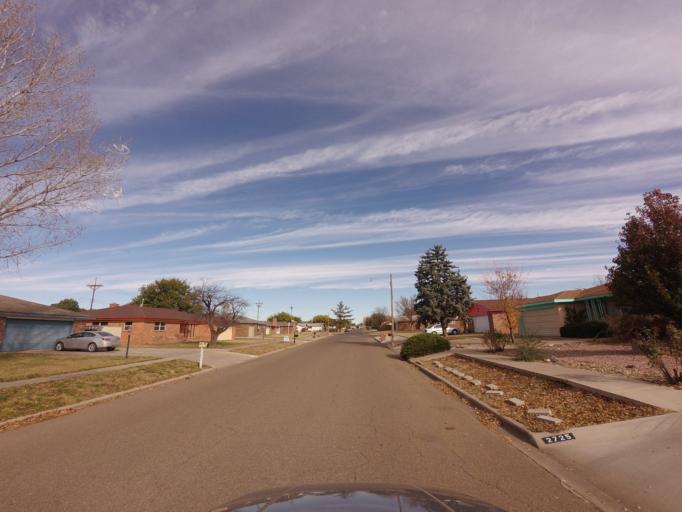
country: US
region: New Mexico
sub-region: Curry County
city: Clovis
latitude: 34.4257
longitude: -103.2225
